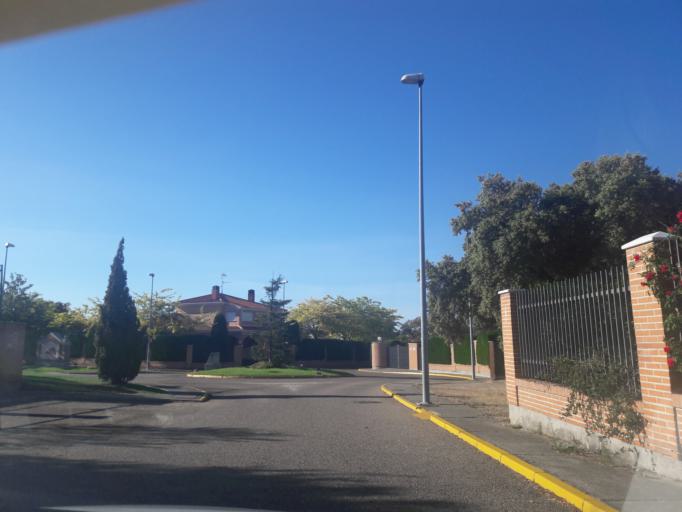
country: ES
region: Castille and Leon
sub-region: Provincia de Salamanca
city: Martinamor
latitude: 40.8096
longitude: -5.6334
